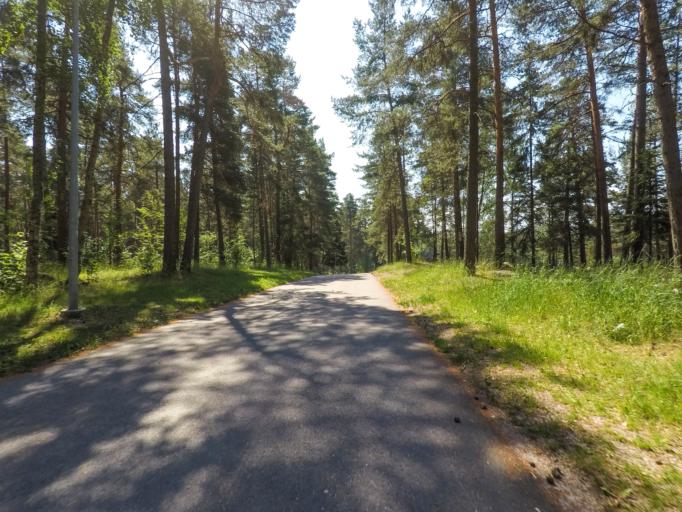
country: FI
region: Uusimaa
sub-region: Helsinki
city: Vantaa
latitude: 60.2182
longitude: 25.1400
